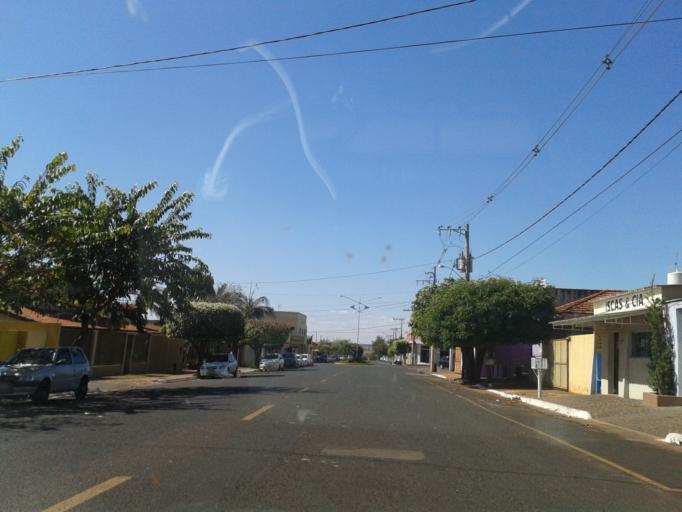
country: BR
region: Minas Gerais
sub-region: Santa Vitoria
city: Santa Vitoria
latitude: -18.8417
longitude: -50.1240
